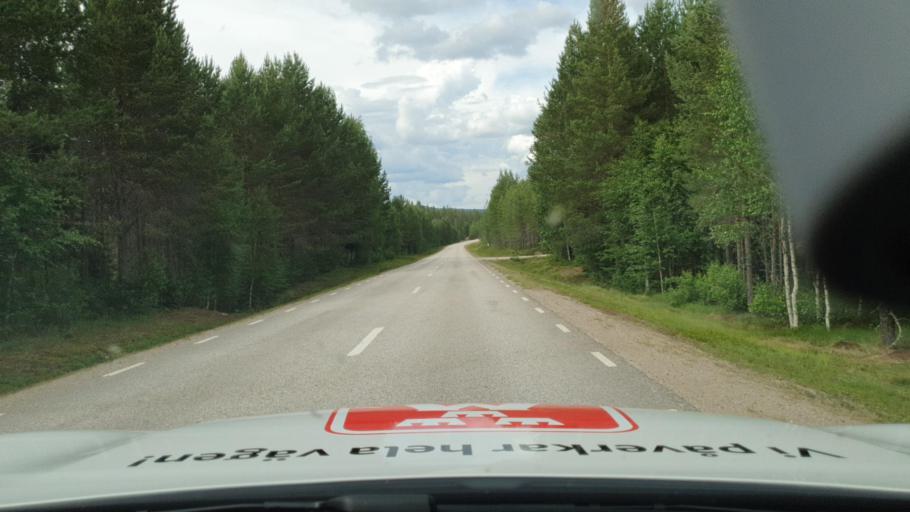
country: NO
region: Hedmark
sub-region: Trysil
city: Innbygda
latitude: 60.9499
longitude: 12.4688
